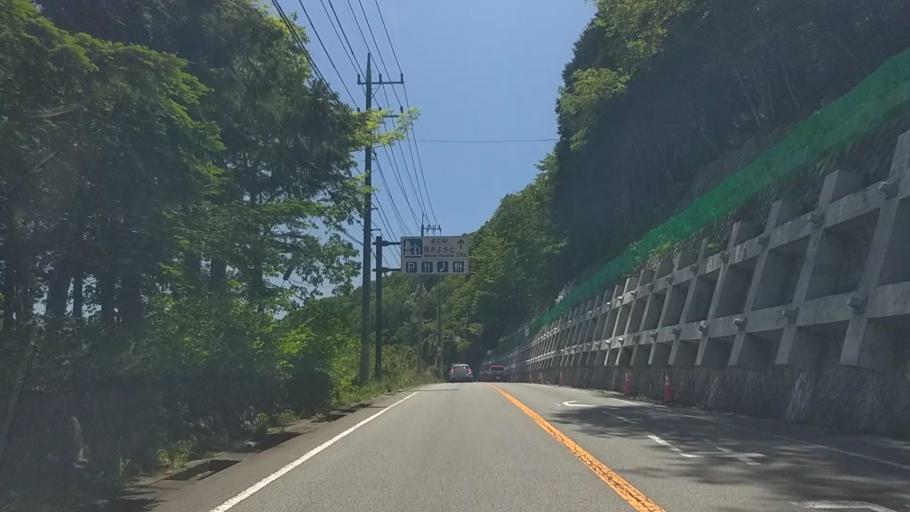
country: JP
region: Yamanashi
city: Nirasaki
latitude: 35.8838
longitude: 138.4265
